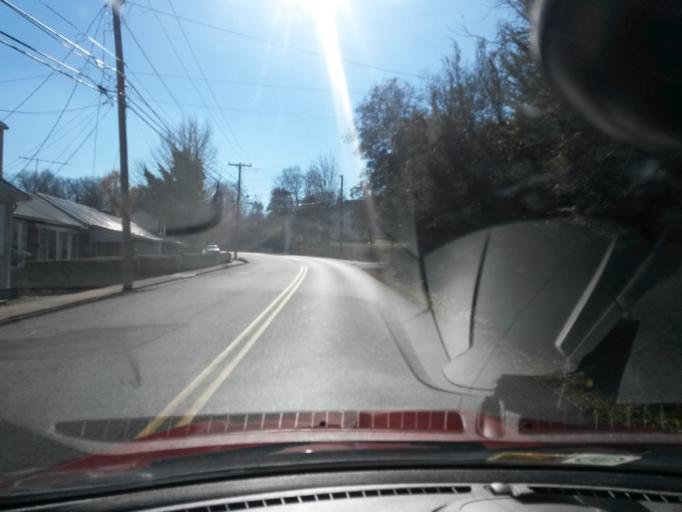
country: US
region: Virginia
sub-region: City of Bedford
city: Bedford
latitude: 37.3419
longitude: -79.5259
